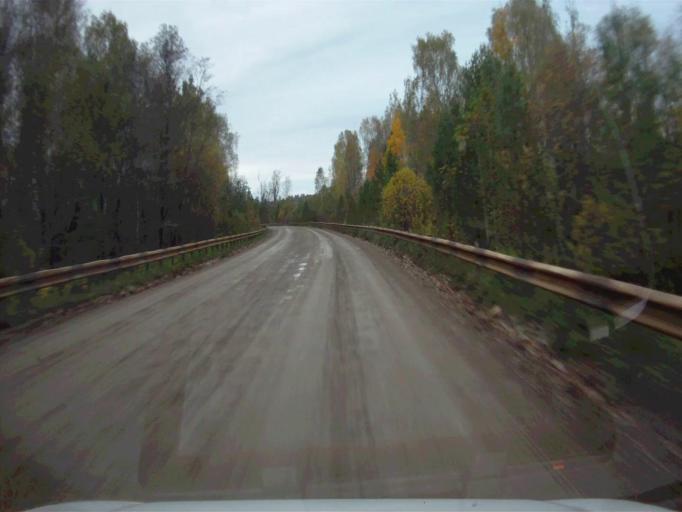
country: RU
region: Chelyabinsk
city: Nyazepetrovsk
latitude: 56.1295
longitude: 59.3279
